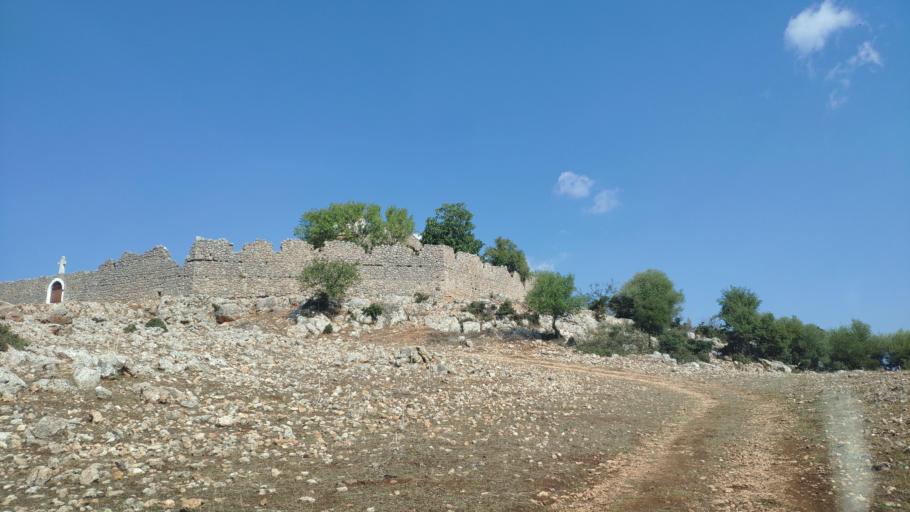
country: GR
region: West Greece
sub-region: Nomos Aitolias kai Akarnanias
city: Fitiai
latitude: 38.6830
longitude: 21.1398
